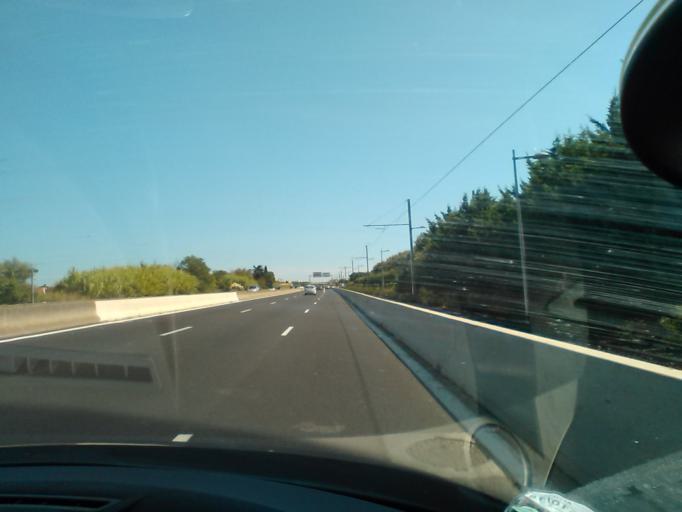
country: FR
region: Languedoc-Roussillon
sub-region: Departement de l'Herault
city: Perols
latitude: 43.5618
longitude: 3.9605
